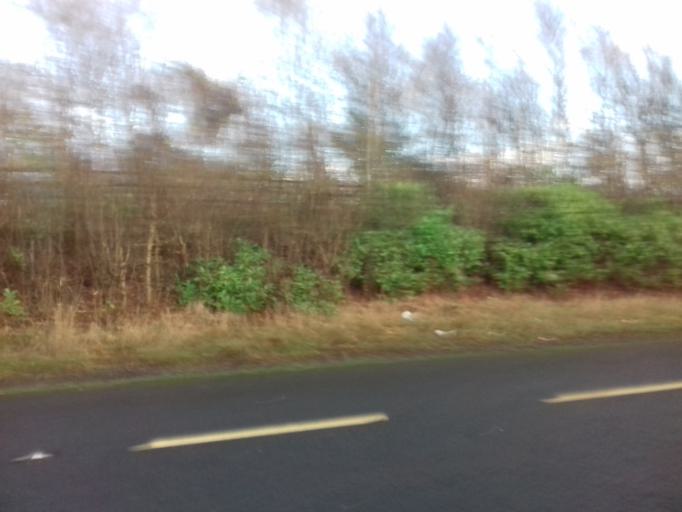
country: IE
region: Leinster
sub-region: Lu
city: Ardee
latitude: 53.8898
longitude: -6.5769
